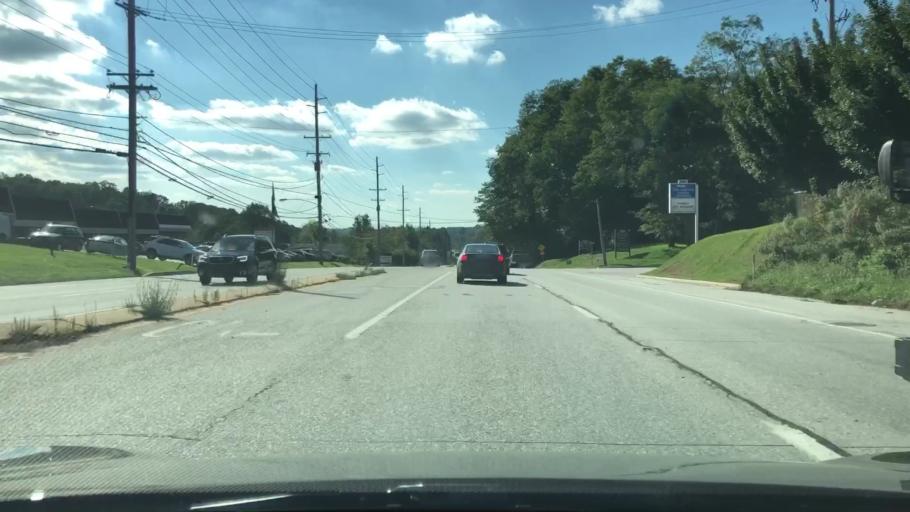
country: US
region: Pennsylvania
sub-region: Delaware County
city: Lima
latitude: 39.9745
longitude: -75.4522
